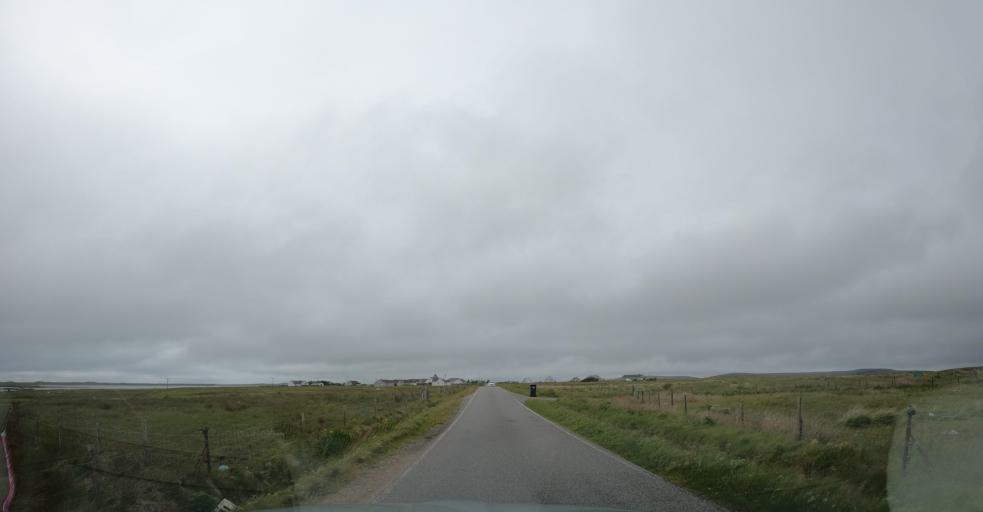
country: GB
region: Scotland
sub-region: Eilean Siar
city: Isle of North Uist
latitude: 57.5680
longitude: -7.3896
